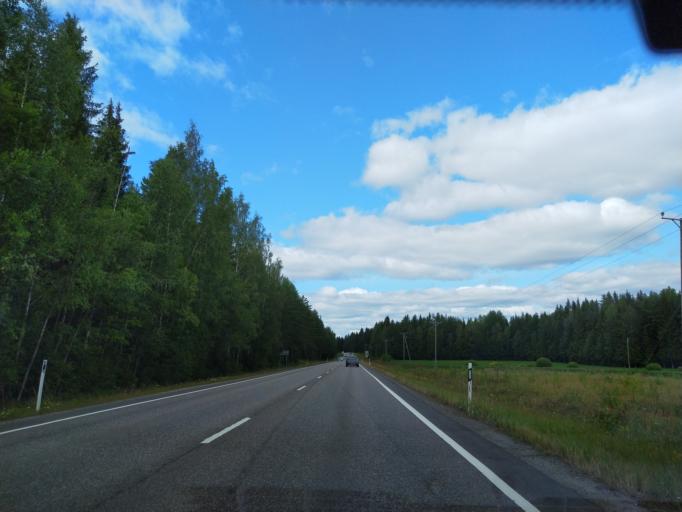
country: FI
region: Haeme
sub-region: Haemeenlinna
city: Renko
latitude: 60.7557
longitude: 24.3004
